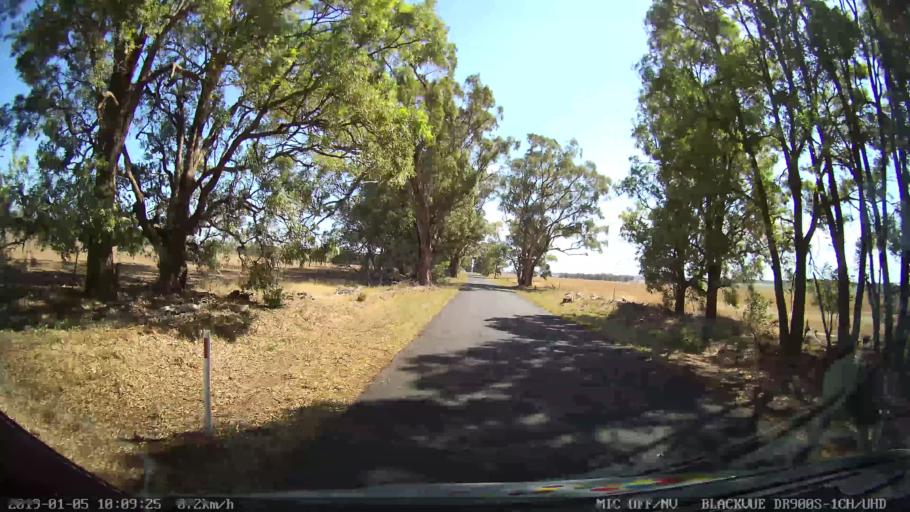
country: AU
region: New South Wales
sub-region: Gilgandra
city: Gilgandra
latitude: -31.6316
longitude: 148.8867
